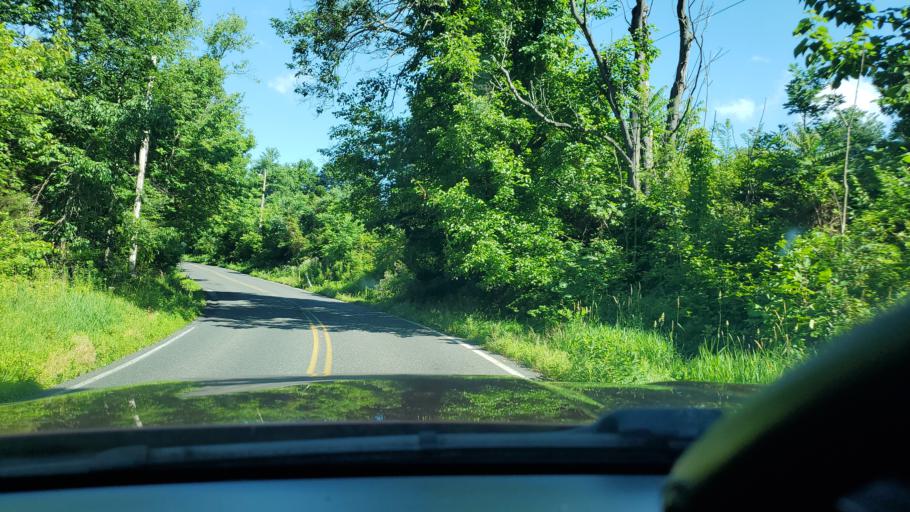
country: US
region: Pennsylvania
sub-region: Montgomery County
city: Pennsburg
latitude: 40.3725
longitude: -75.5121
